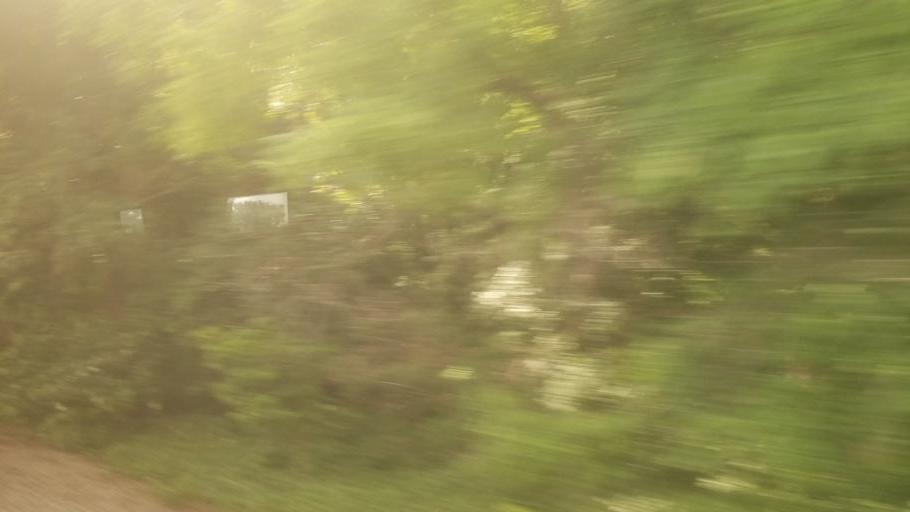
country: US
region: Kansas
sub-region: Johnson County
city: De Soto
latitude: 38.9800
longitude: -95.0008
